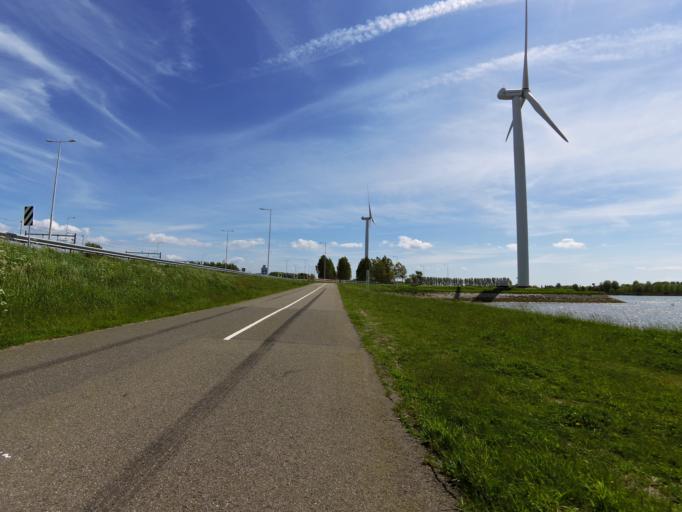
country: NL
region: South Holland
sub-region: Gemeente Brielle
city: Brielle
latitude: 51.9245
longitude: 4.1737
